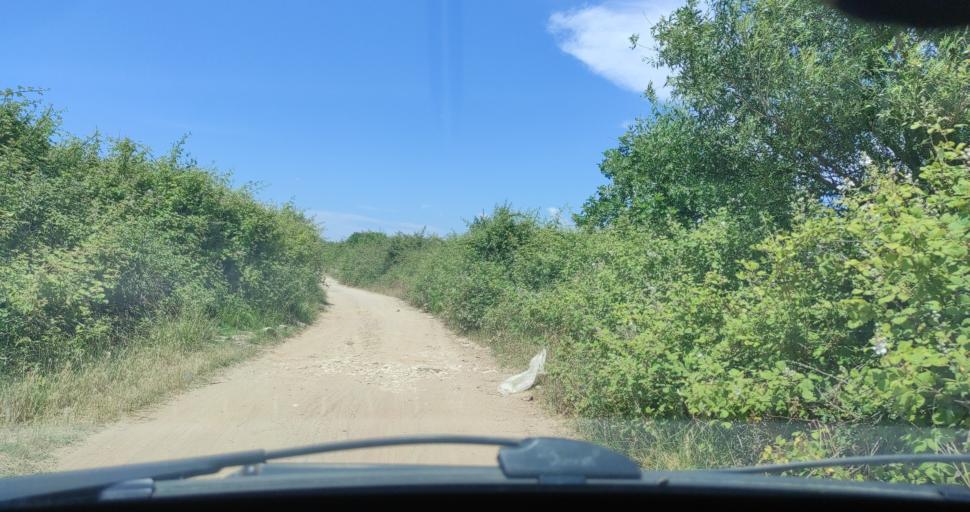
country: AL
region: Shkoder
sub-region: Rrethi i Shkodres
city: Velipoje
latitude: 41.8822
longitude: 19.3926
